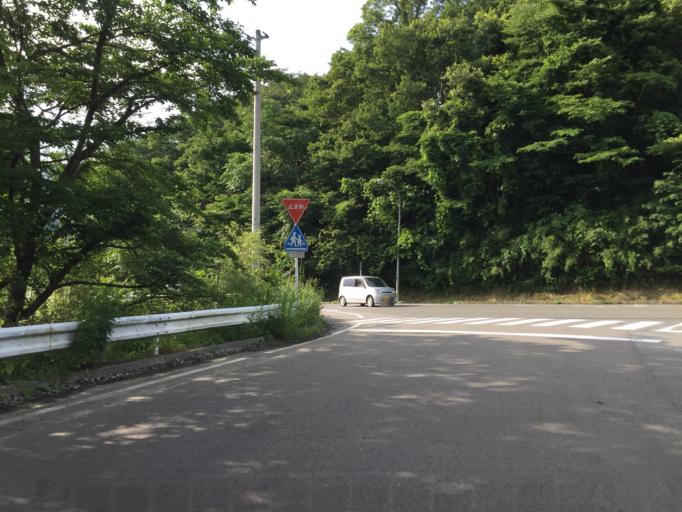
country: JP
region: Fukushima
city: Fukushima-shi
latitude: 37.6867
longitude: 140.5257
